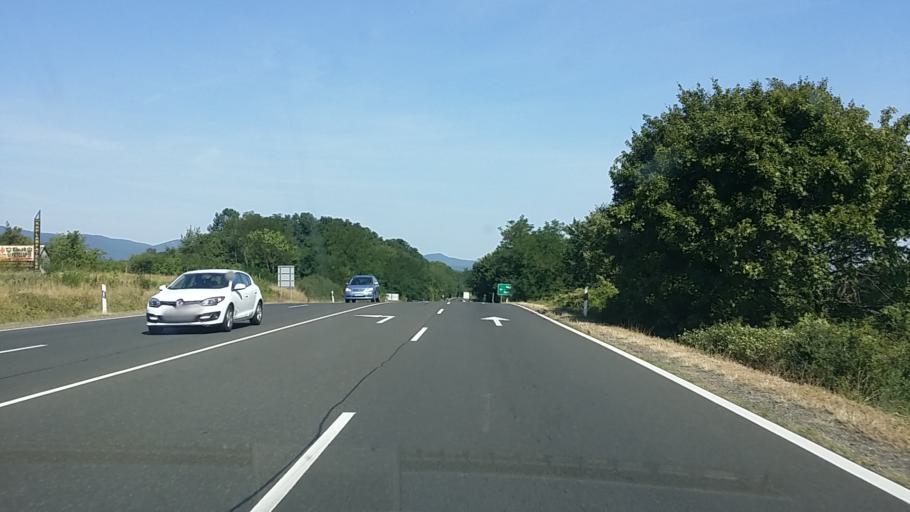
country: HU
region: Nograd
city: Retsag
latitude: 47.8837
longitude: 19.1042
